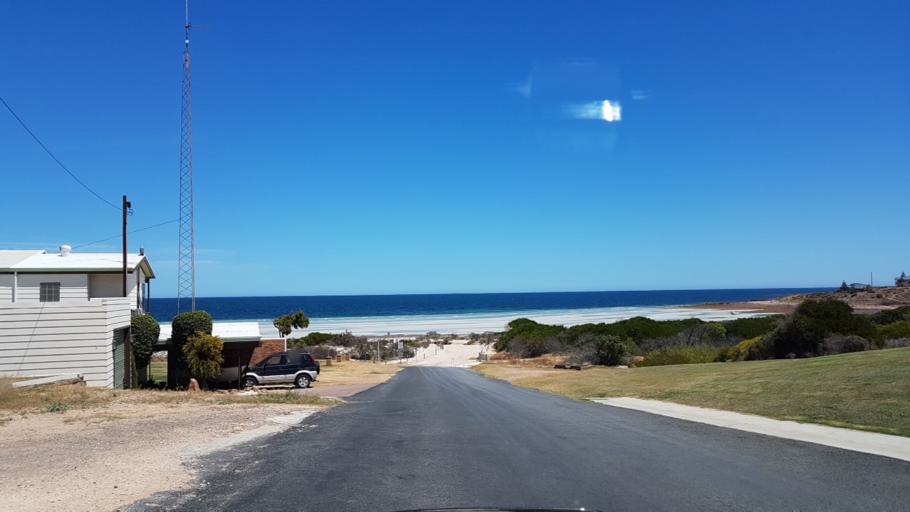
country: AU
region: South Australia
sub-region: Copper Coast
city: Wallaroo
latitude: -33.8968
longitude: 137.6285
